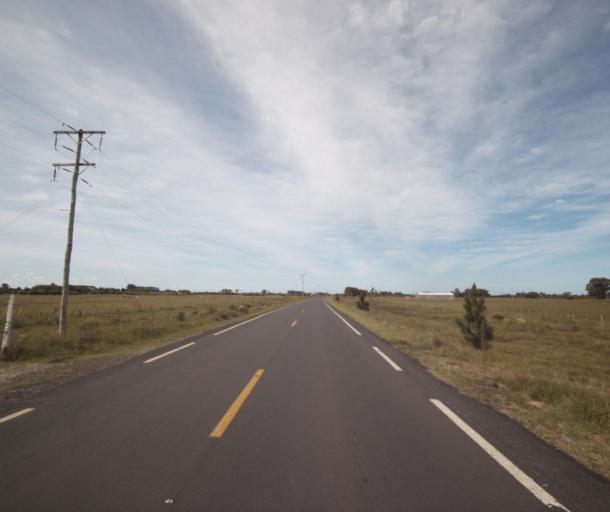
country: BR
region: Rio Grande do Sul
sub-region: Rio Grande
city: Rio Grande
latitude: -31.9277
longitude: -51.9579
